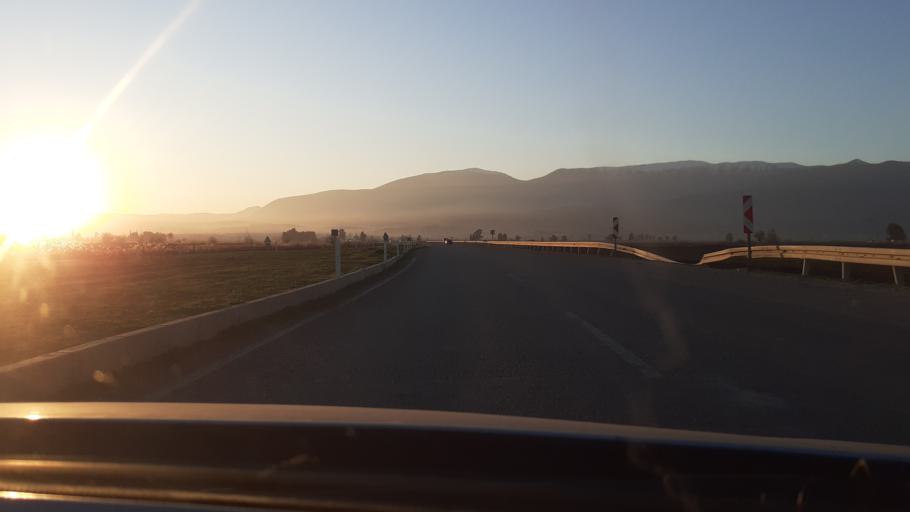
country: TR
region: Hatay
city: Kirikhan
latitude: 36.5069
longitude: 36.4339
